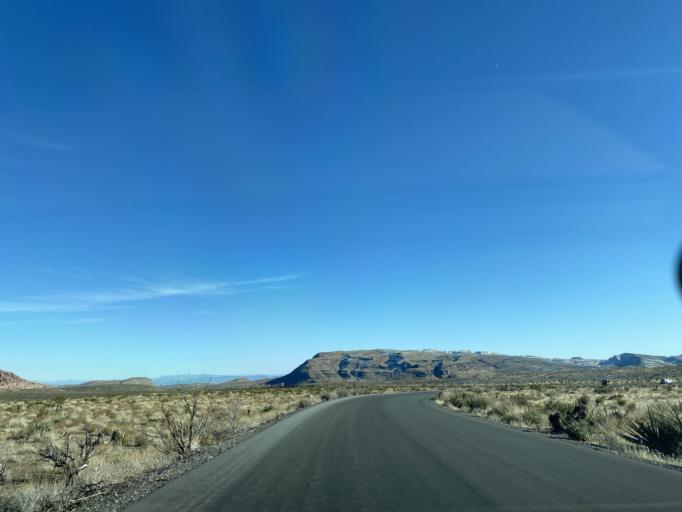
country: US
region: Nevada
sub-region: Clark County
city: Summerlin South
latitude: 36.1397
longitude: -115.4650
